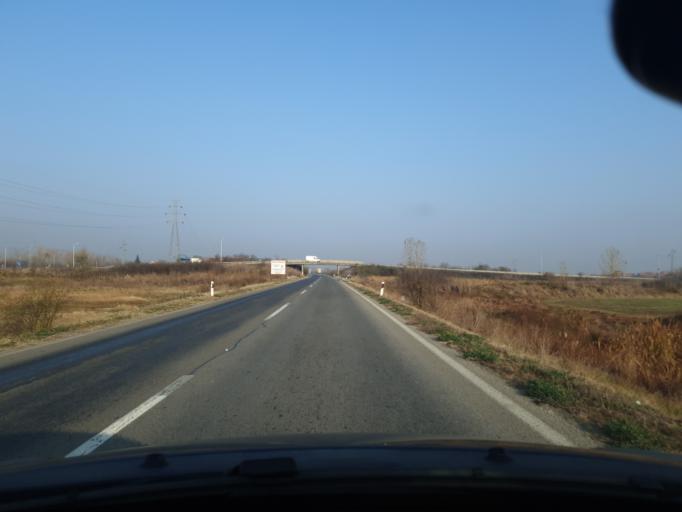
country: RS
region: Central Serbia
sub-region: Jablanicki Okrug
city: Leskovac
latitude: 42.9958
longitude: 21.9705
